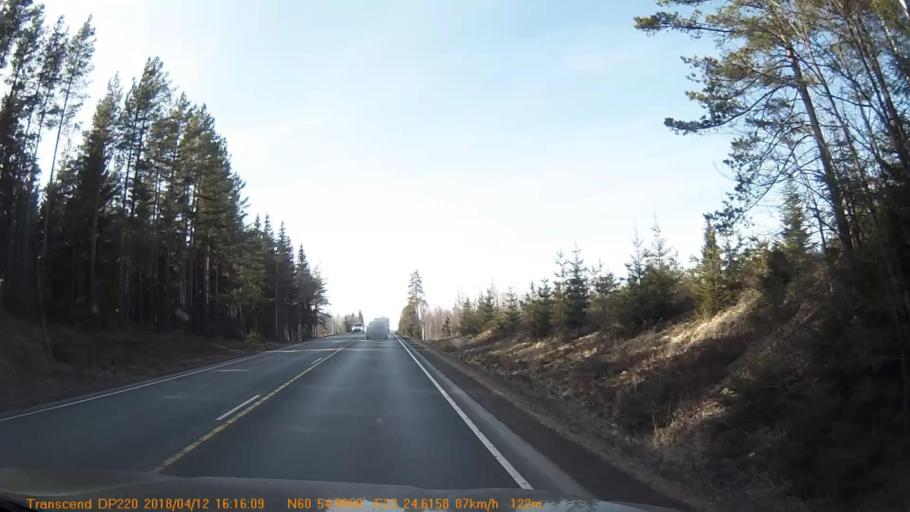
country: FI
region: Haeme
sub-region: Forssa
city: Humppila
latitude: 60.9150
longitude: 23.4101
